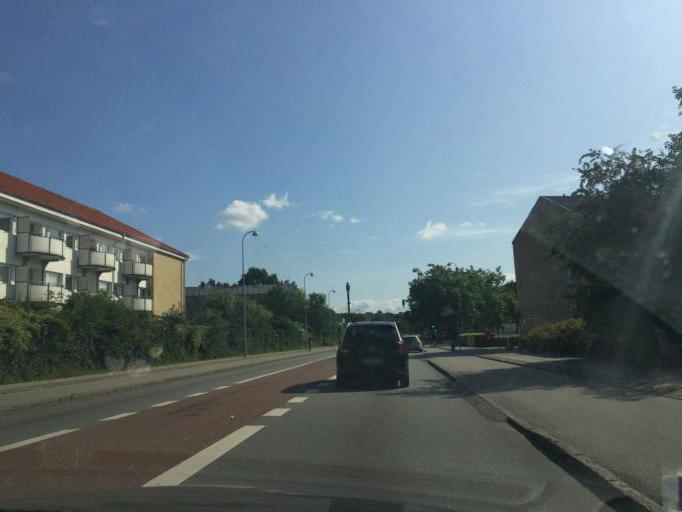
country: DK
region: Capital Region
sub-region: Herlev Kommune
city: Herlev
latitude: 55.7210
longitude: 12.4712
